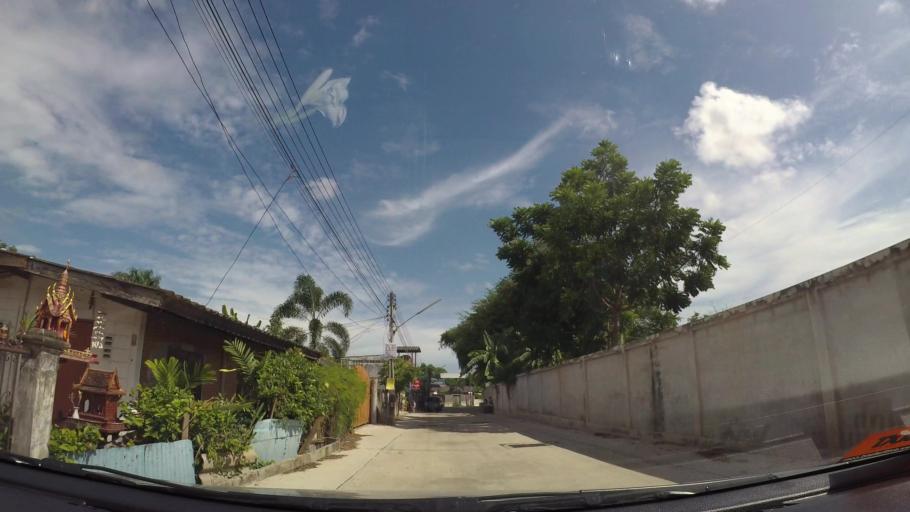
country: TH
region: Chon Buri
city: Sattahip
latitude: 12.6909
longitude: 100.8946
